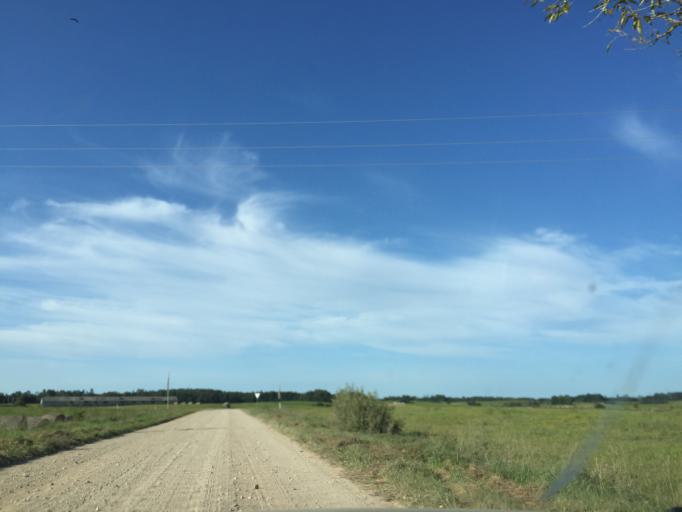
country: LT
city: Zarasai
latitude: 55.8052
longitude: 25.9477
